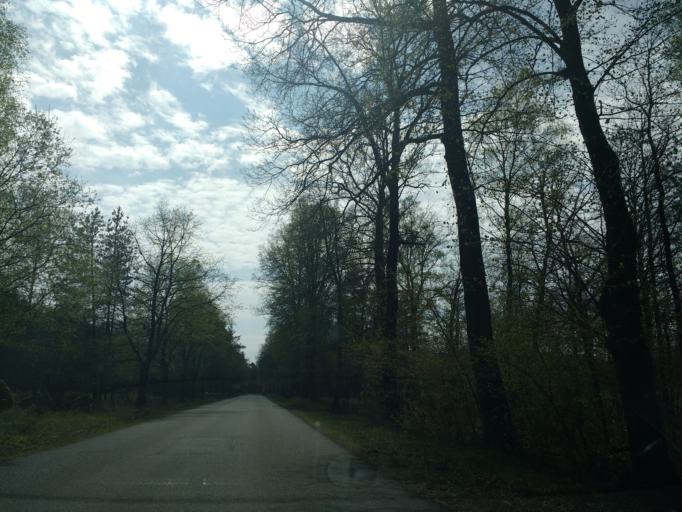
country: DE
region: North Rhine-Westphalia
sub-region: Regierungsbezirk Detmold
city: Hovelhof
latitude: 51.8032
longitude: 8.7223
